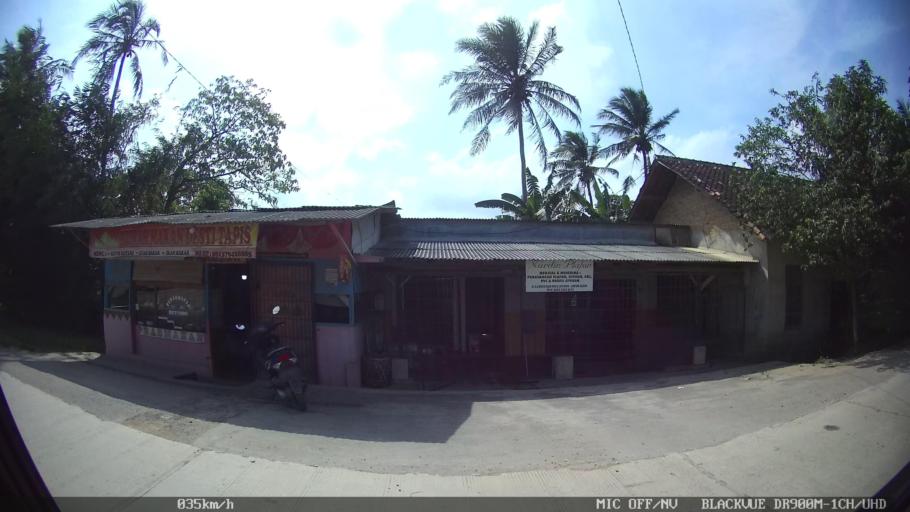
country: ID
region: Lampung
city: Kedaton
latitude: -5.3487
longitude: 105.2660
